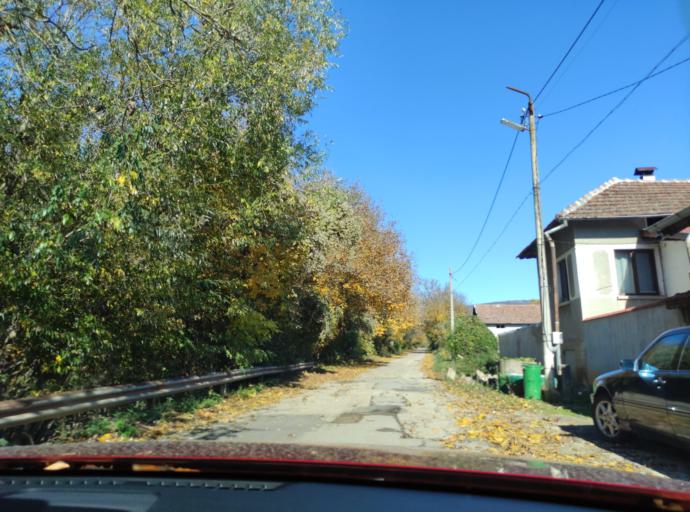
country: BG
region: Montana
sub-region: Obshtina Montana
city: Montana
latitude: 43.4221
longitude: 23.0653
